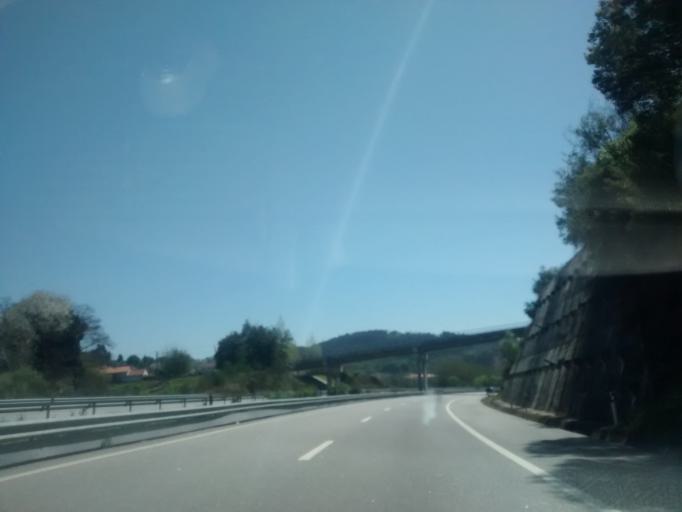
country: PT
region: Braga
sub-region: Guimaraes
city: Candoso
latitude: 41.4188
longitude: -8.3262
